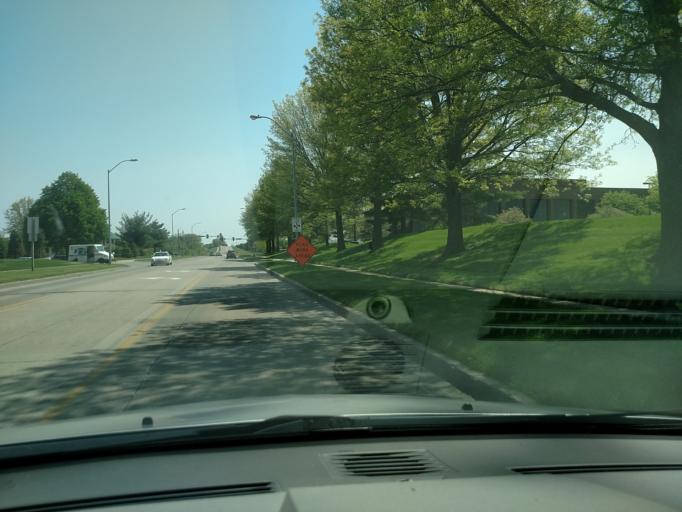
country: US
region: Iowa
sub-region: Polk County
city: Clive
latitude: 41.5972
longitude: -93.7617
